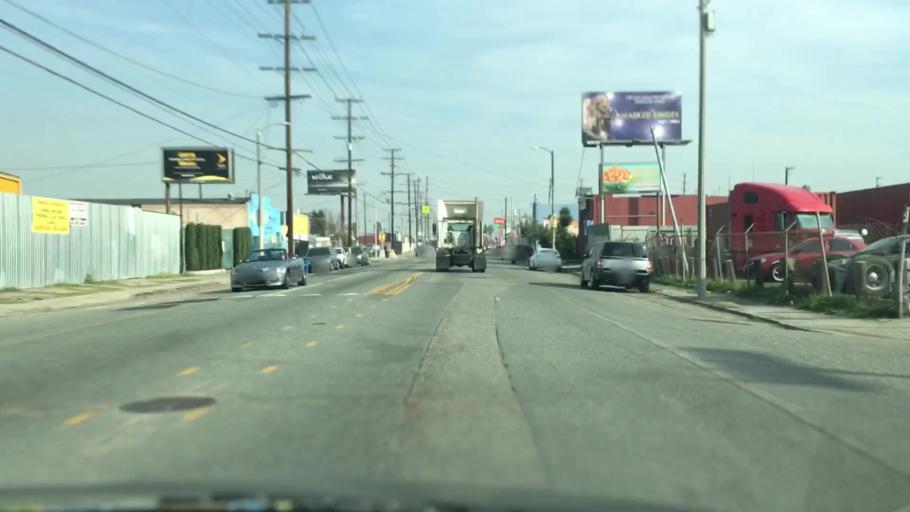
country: US
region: California
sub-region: Los Angeles County
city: West Carson
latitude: 33.7807
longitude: -118.2495
